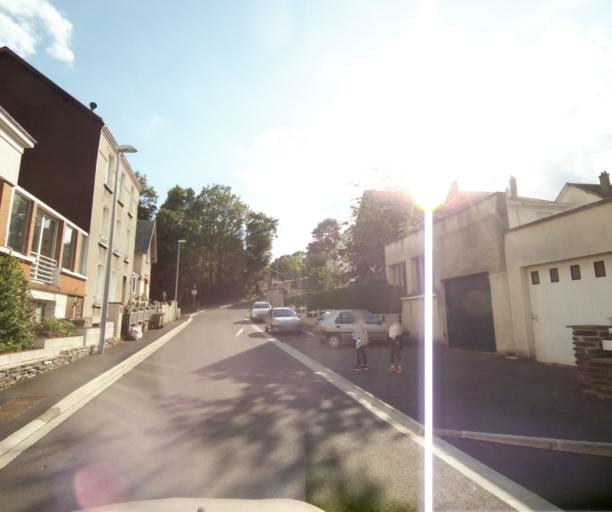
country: FR
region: Champagne-Ardenne
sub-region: Departement des Ardennes
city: Montcy-Notre-Dame
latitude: 49.7769
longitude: 4.7304
